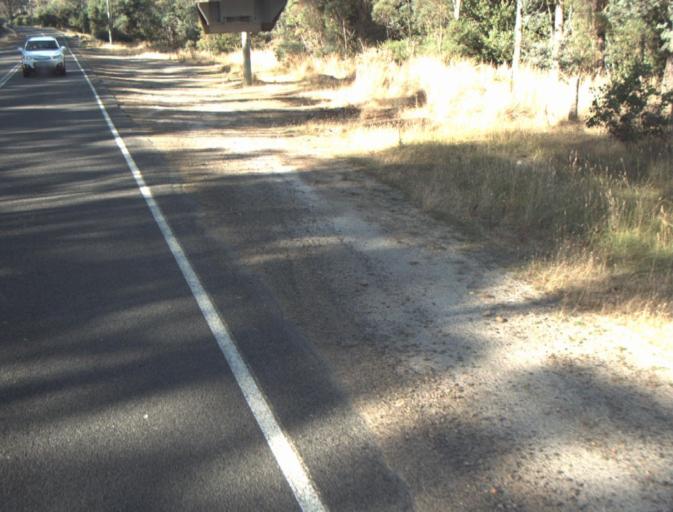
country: AU
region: Tasmania
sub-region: Launceston
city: Newstead
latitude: -41.4222
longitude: 147.2559
